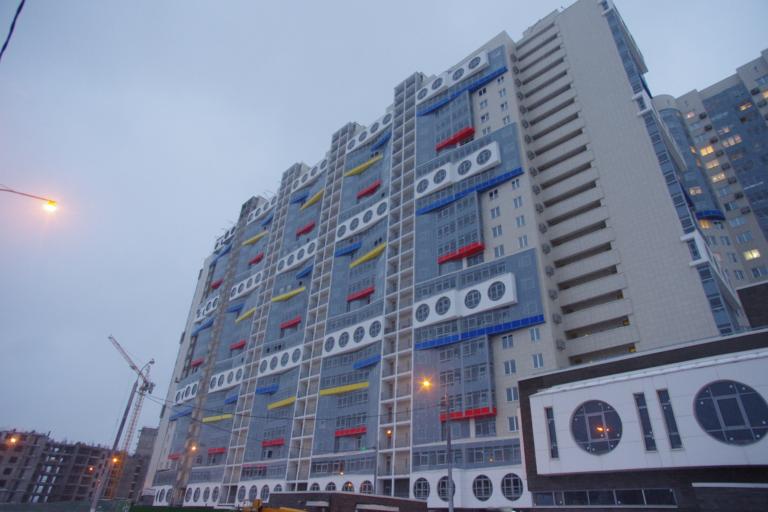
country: RU
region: Moskovskaya
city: Pavshino
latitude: 55.8280
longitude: 37.3690
